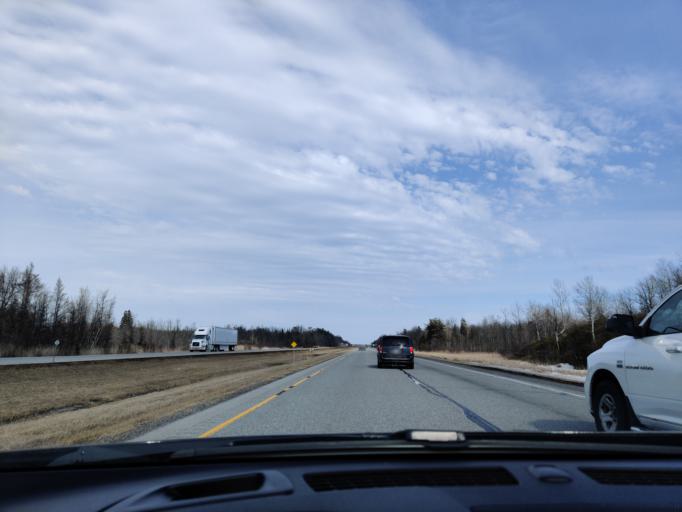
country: US
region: New York
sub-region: St. Lawrence County
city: Ogdensburg
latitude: 44.8439
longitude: -75.3520
